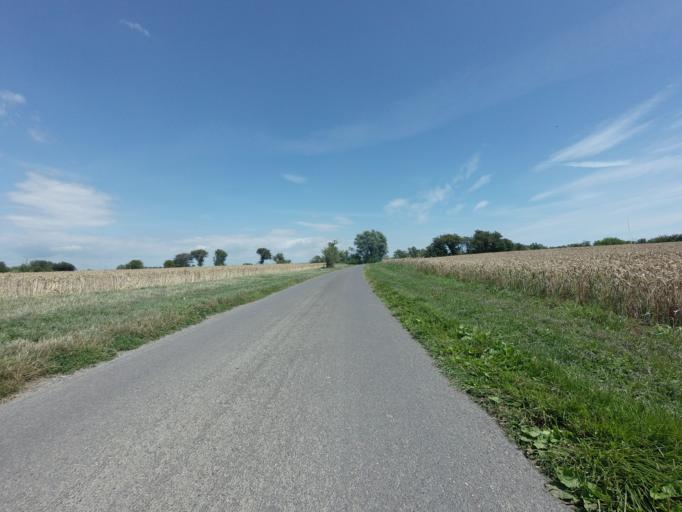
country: GB
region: England
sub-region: Kent
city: Lydd
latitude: 50.9858
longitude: 0.8715
